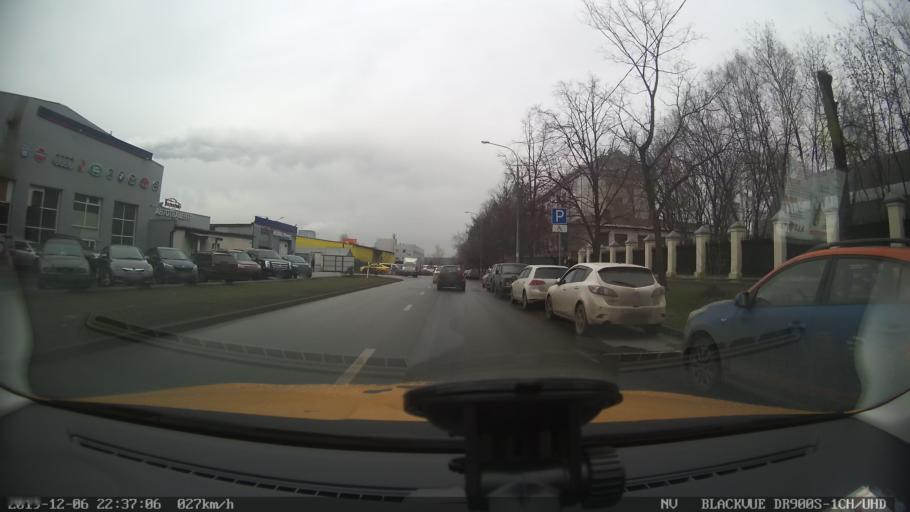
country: RU
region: Moscow
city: Metrogorodok
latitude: 55.8140
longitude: 37.7855
